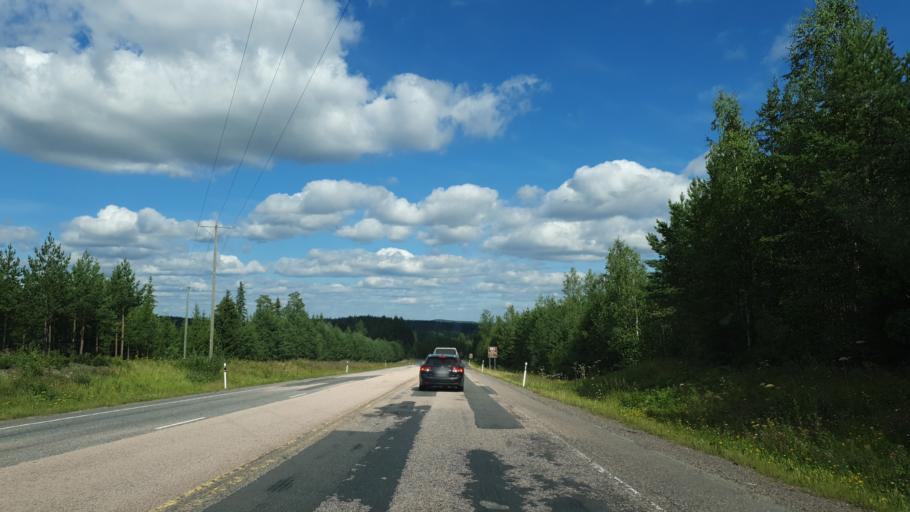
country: FI
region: Central Finland
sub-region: Jaemsae
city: Jaemsae
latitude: 61.8291
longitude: 25.0835
